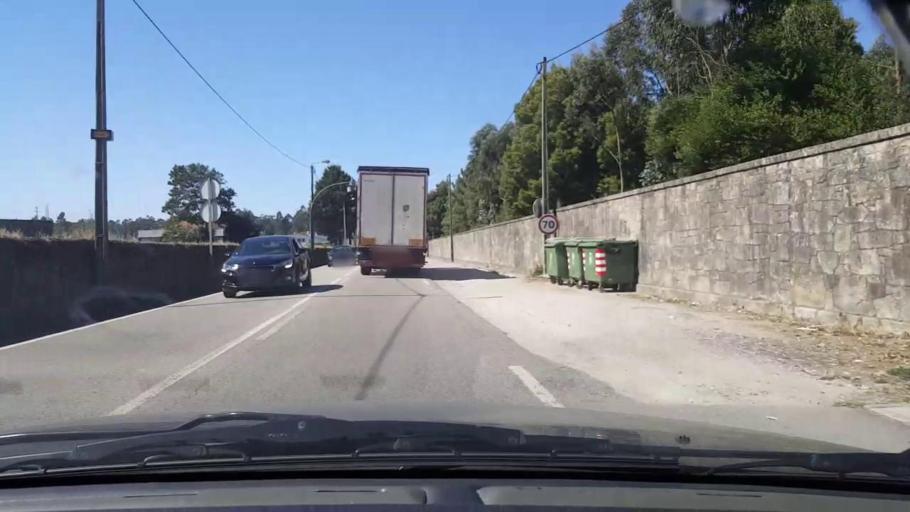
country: PT
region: Porto
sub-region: Vila do Conde
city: Arvore
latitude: 41.3381
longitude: -8.6864
